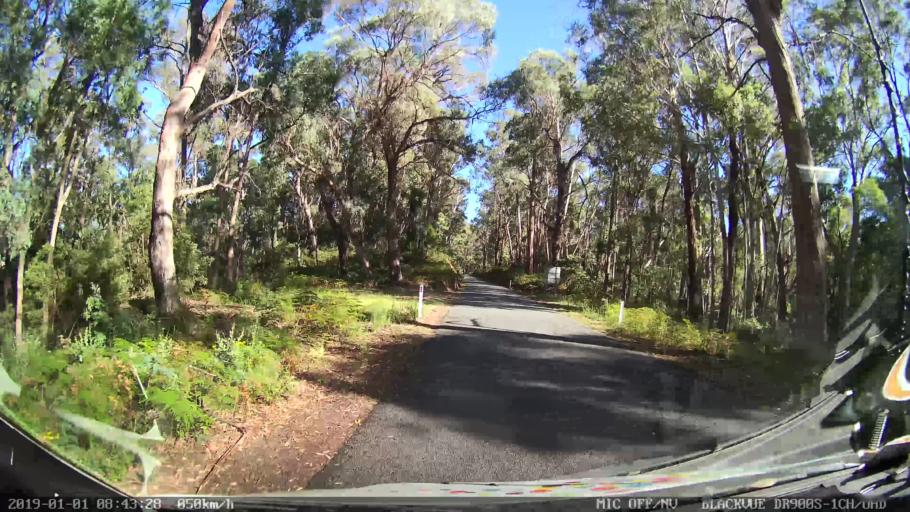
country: AU
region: New South Wales
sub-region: Snowy River
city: Jindabyne
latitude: -36.3170
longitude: 148.1929
